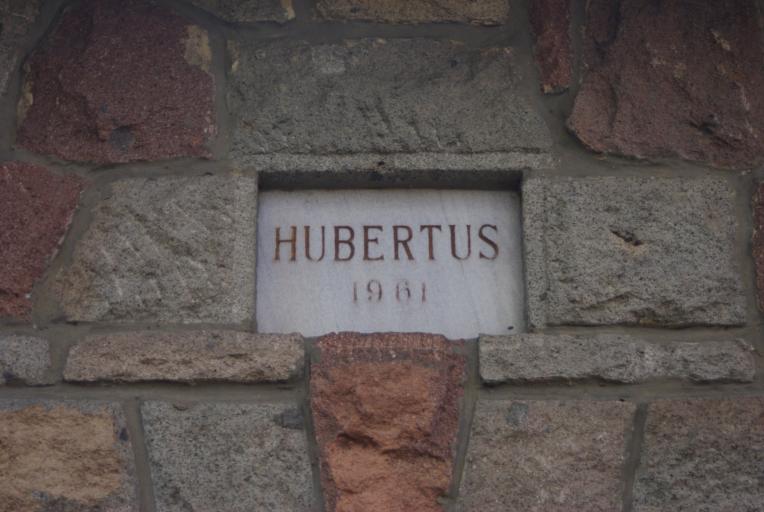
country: HU
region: Pest
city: Pilisszentkereszt
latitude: 47.7365
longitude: 18.9277
